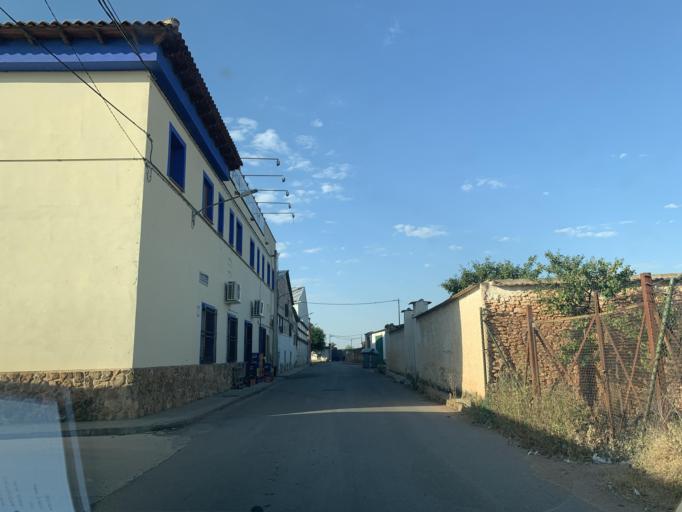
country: ES
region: Castille-La Mancha
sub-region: Provincia de Ciudad Real
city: Argamasilla de Alba
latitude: 39.1695
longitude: -3.2300
